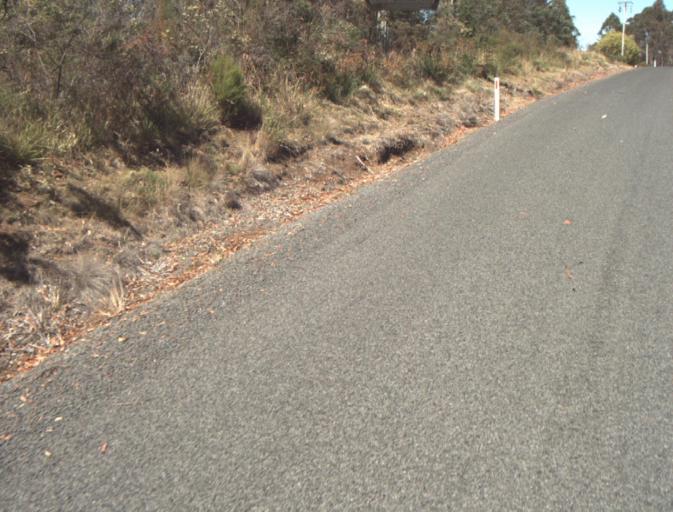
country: AU
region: Tasmania
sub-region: Launceston
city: Newstead
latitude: -41.3696
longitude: 147.2998
